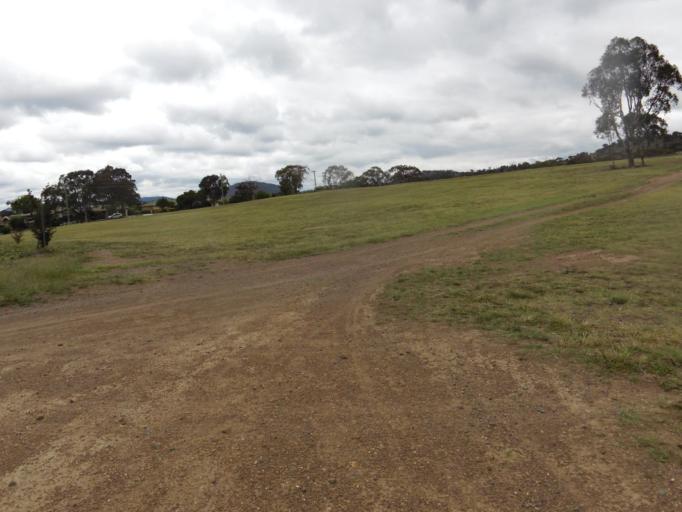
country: AU
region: Australian Capital Territory
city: Macquarie
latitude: -35.3441
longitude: 149.0272
